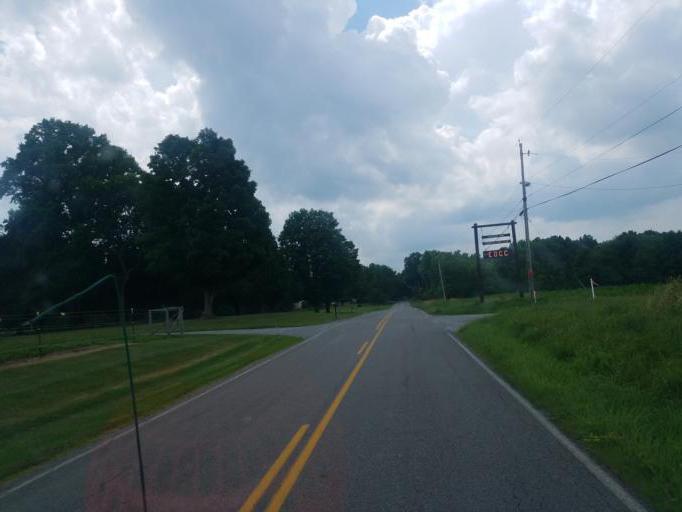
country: US
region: Ohio
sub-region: Columbiana County
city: Salem
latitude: 40.9731
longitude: -80.8463
